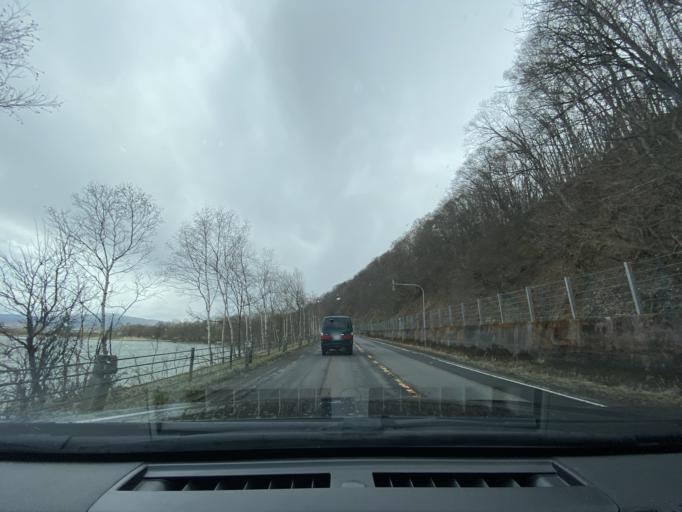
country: JP
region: Hokkaido
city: Fukagawa
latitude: 43.7033
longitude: 142.0812
